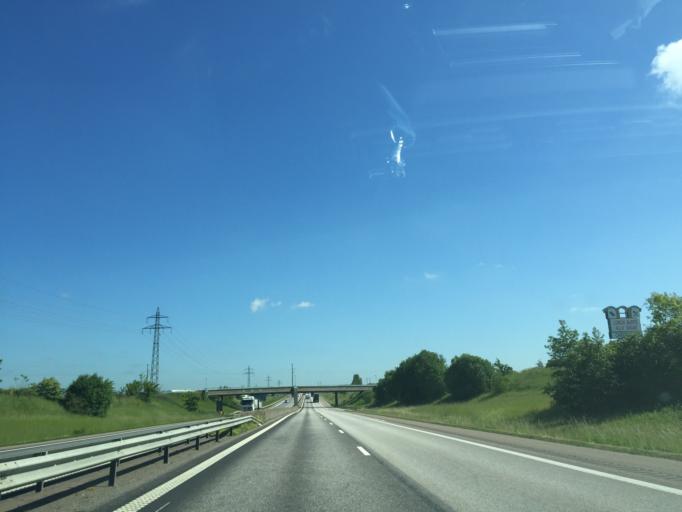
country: SE
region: Skane
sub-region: Astorps Kommun
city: Astorp
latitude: 56.1270
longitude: 12.9116
